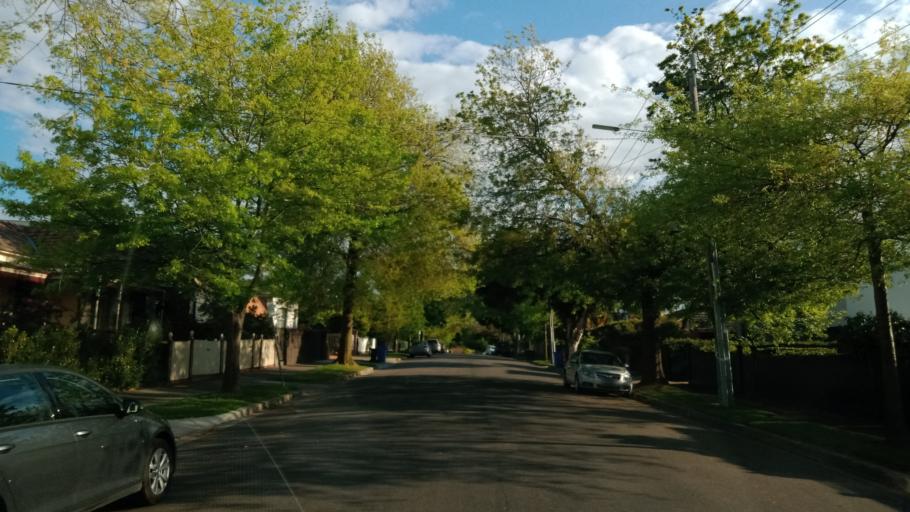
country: AU
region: Victoria
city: Glenferrie
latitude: -37.8314
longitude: 145.0502
